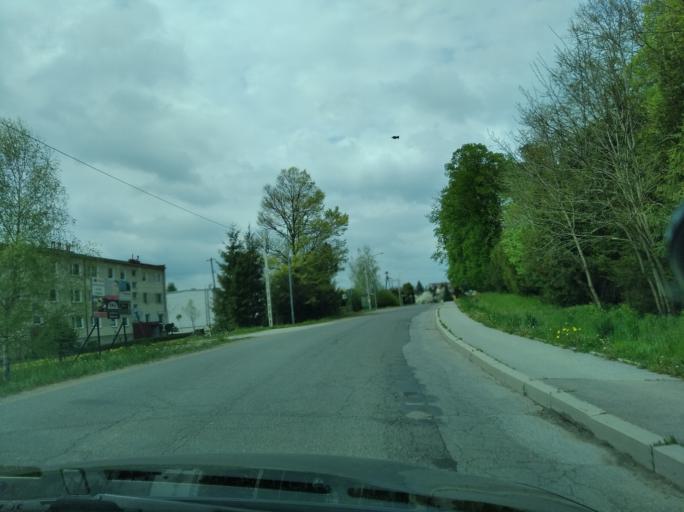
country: PL
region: Subcarpathian Voivodeship
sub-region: Powiat brzozowski
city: Jasionow
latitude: 49.6439
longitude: 21.9478
